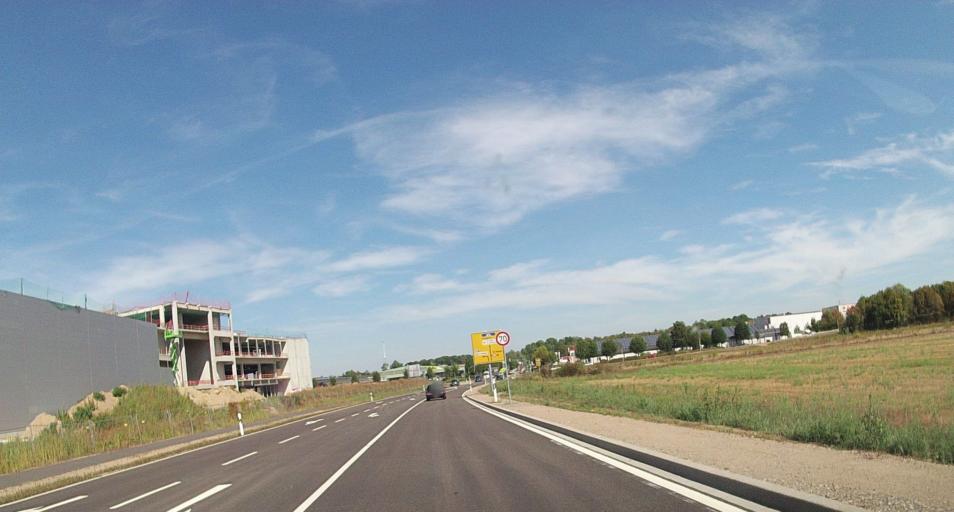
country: DE
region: Baden-Wuerttemberg
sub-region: Karlsruhe Region
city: Rastatt
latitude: 48.8572
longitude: 8.2373
